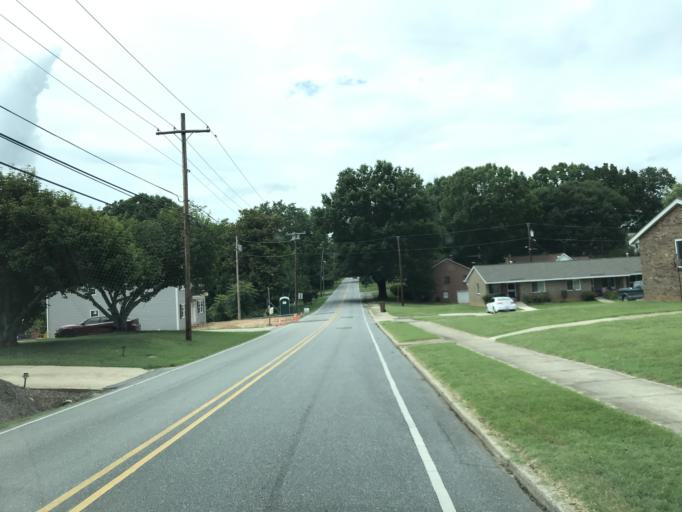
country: US
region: North Carolina
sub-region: Lincoln County
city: Lincolnton
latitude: 35.4769
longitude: -81.2494
